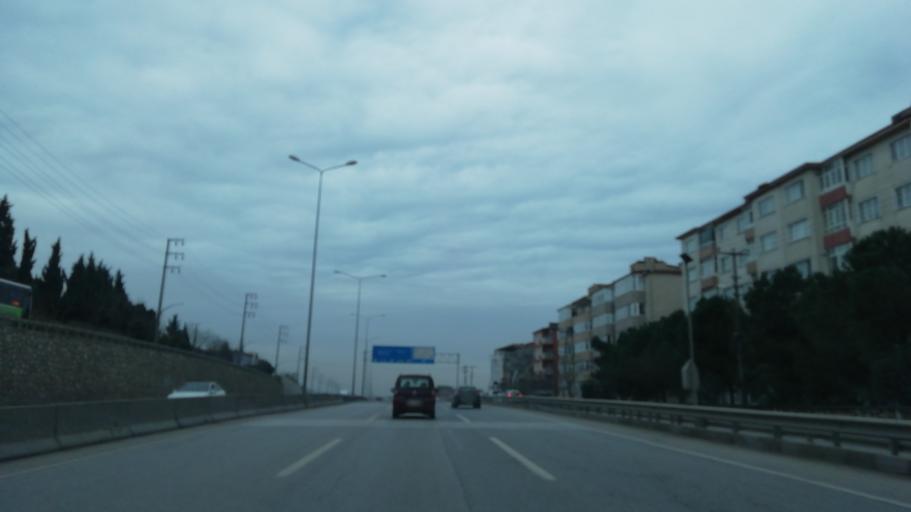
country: TR
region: Kocaeli
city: Derince
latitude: 40.7566
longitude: 29.8110
